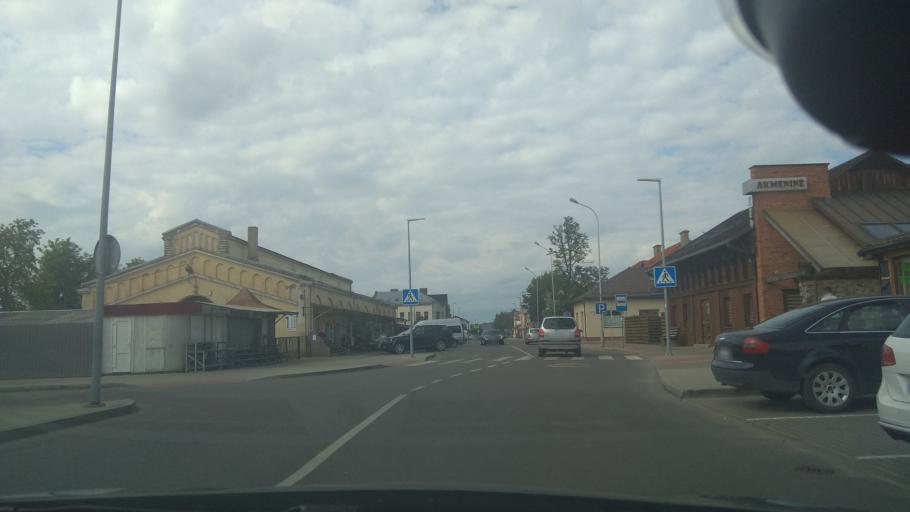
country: LT
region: Marijampoles apskritis
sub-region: Marijampole Municipality
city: Marijampole
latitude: 54.5534
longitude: 23.3538
